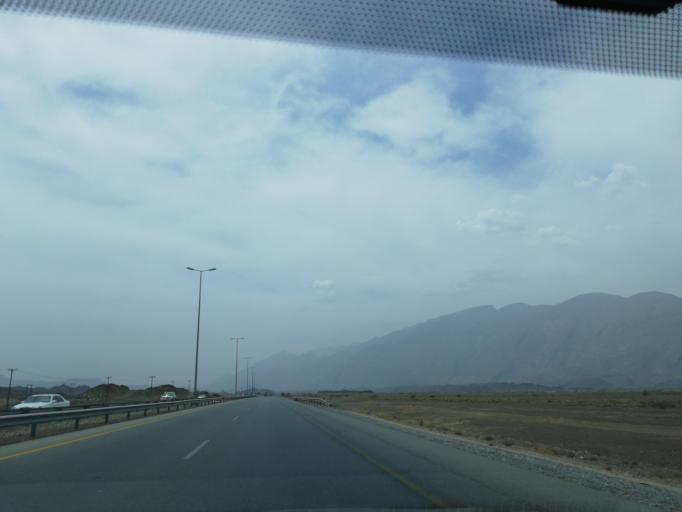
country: OM
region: Muhafazat ad Dakhiliyah
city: Sufalat Sama'il
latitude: 23.2603
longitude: 57.9328
